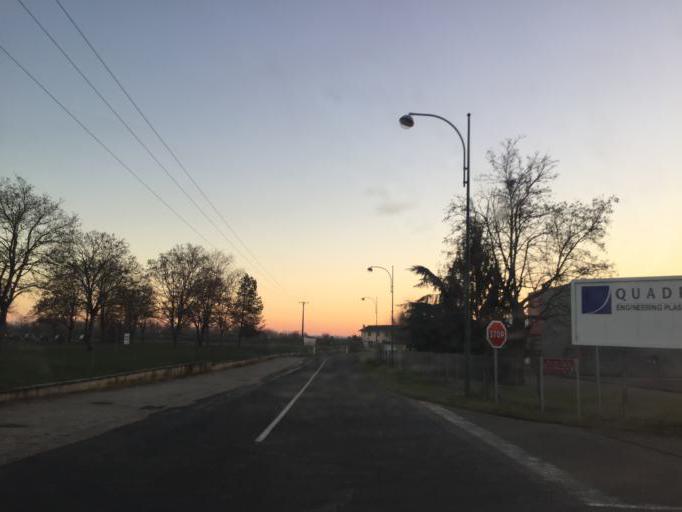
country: FR
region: Rhone-Alpes
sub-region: Departement de l'Ain
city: Balan
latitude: 45.8444
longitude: 5.1140
